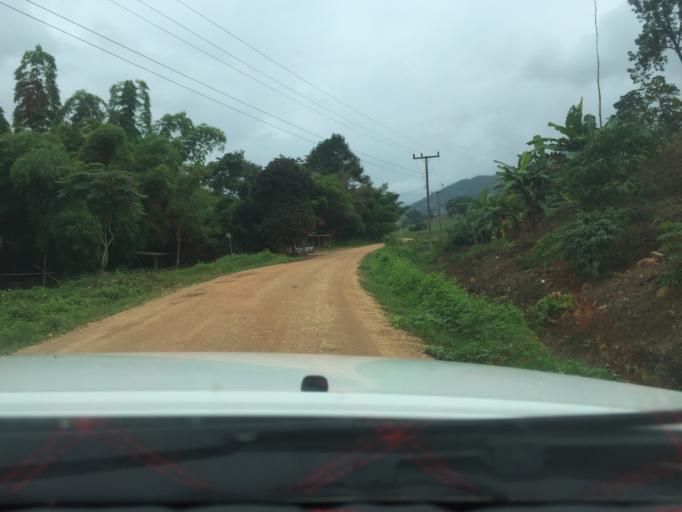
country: TH
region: Phayao
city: Phu Sang
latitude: 19.6795
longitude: 100.5033
